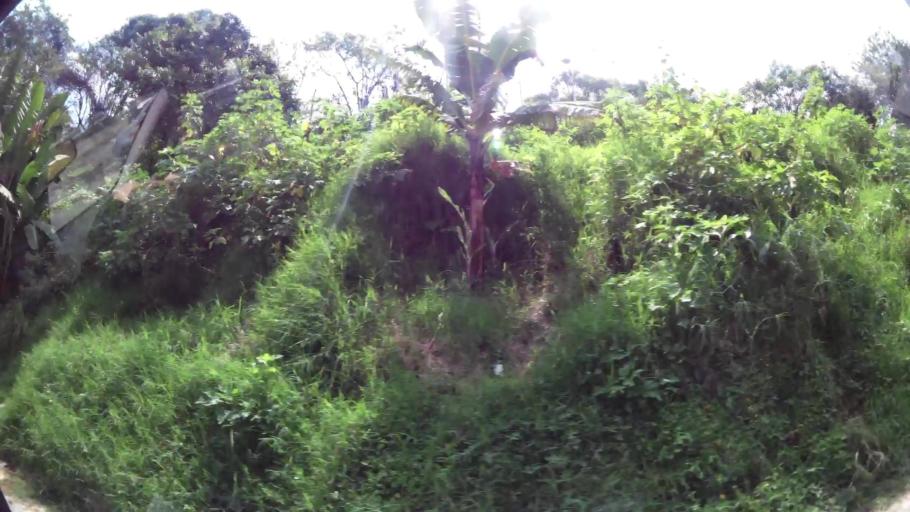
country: CO
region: Antioquia
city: Medellin
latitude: 6.2493
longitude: -75.6189
